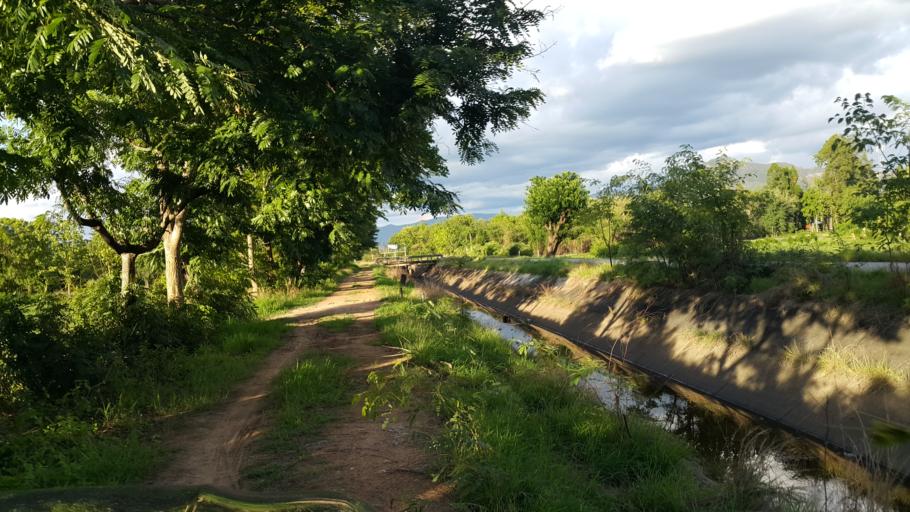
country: TH
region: Chiang Mai
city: San Kamphaeng
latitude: 18.7270
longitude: 99.1910
